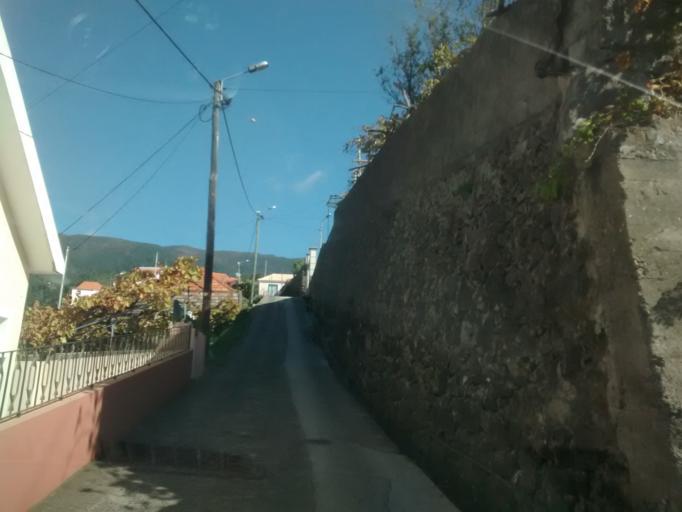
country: PT
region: Madeira
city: Calheta
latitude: 32.7268
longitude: -17.1664
